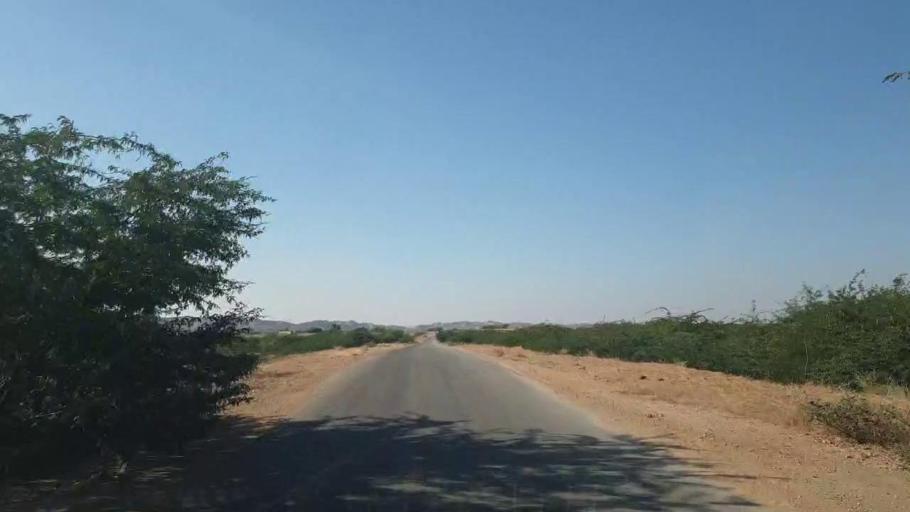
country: PK
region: Sindh
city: Malir Cantonment
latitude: 25.2834
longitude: 67.5799
